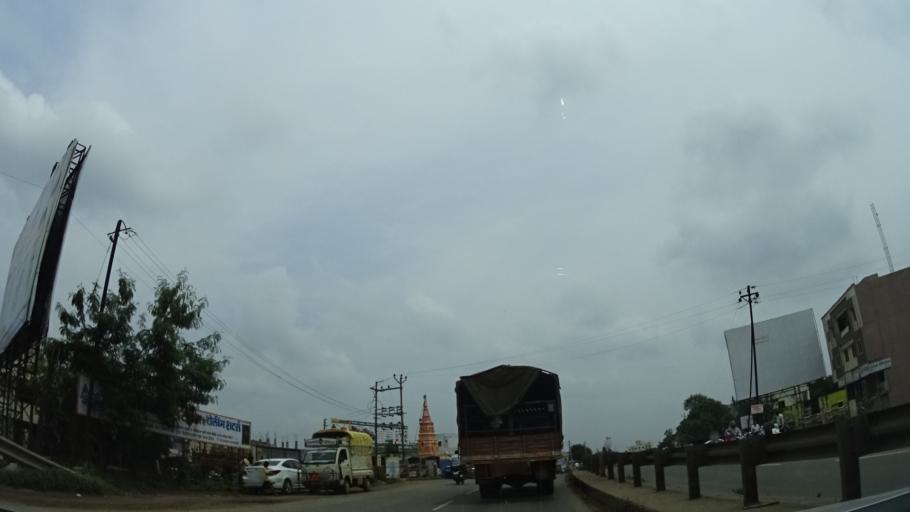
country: IN
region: Maharashtra
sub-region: Pune Division
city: Koregaon
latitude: 18.6997
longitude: 74.1430
